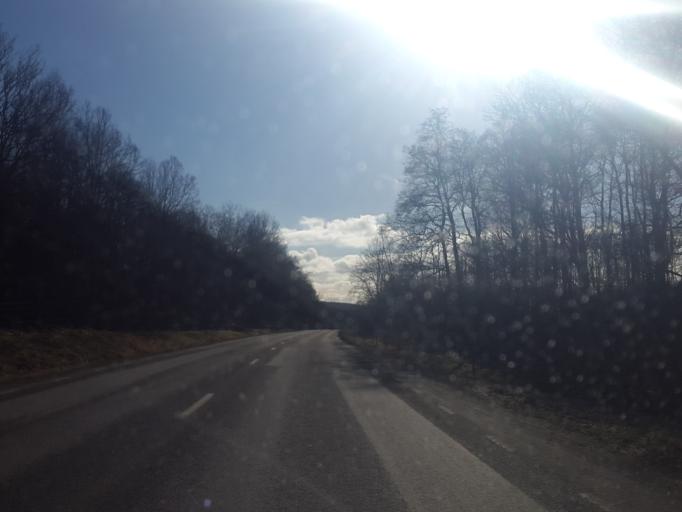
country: SE
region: Vaestra Goetaland
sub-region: Alingsas Kommun
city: Alingsas
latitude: 57.9674
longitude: 12.4444
